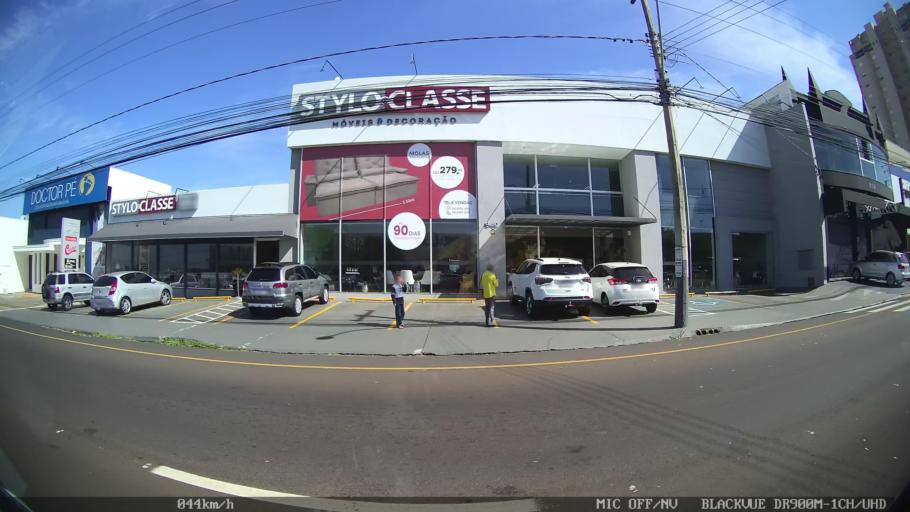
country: BR
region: Sao Paulo
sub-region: Franca
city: Franca
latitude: -20.5488
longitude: -47.4174
